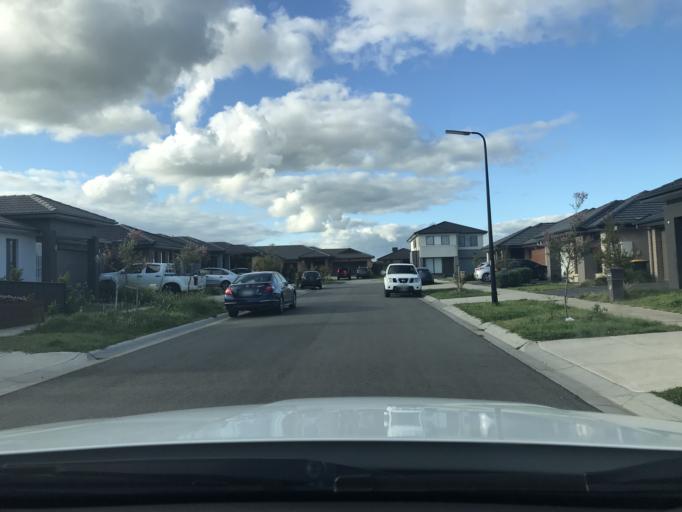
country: AU
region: Victoria
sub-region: Hume
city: Roxburgh Park
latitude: -37.5907
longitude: 144.8966
